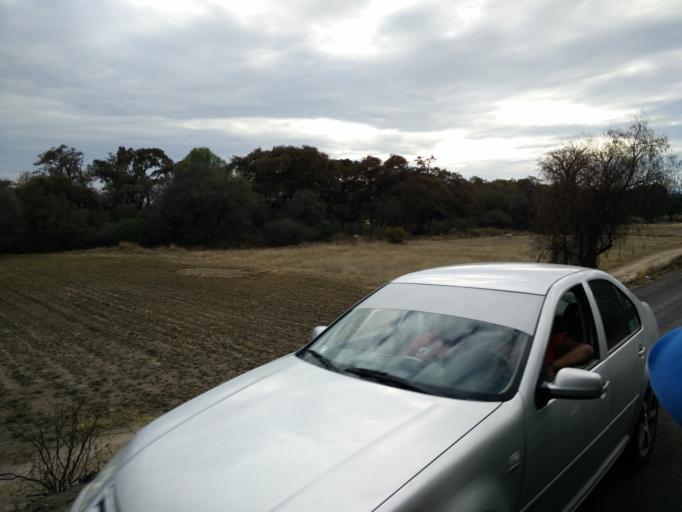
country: MX
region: Queretaro
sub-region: Tequisquiapan
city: Tequisquiapan
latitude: 20.5373
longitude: -99.8861
